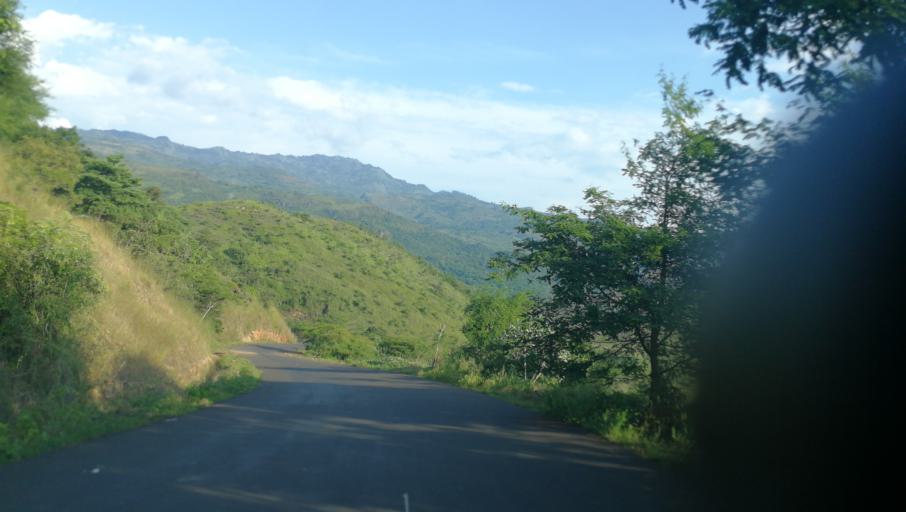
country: ET
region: Southern Nations, Nationalities, and People's Region
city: Areka
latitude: 6.8266
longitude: 37.3022
